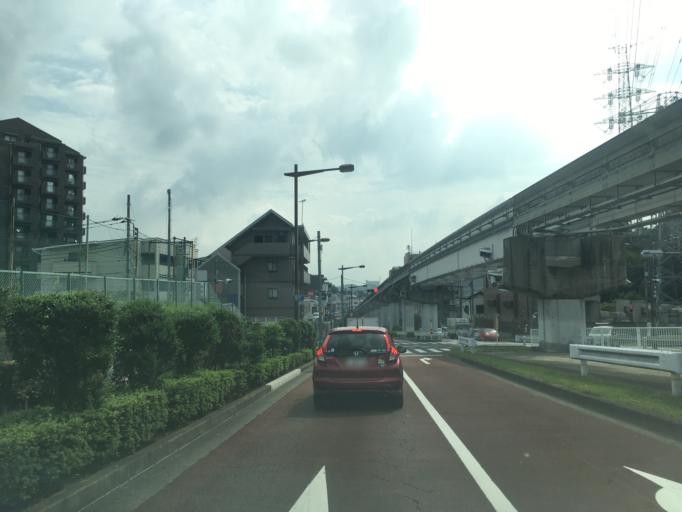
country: JP
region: Tokyo
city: Hino
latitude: 35.6418
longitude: 139.4094
